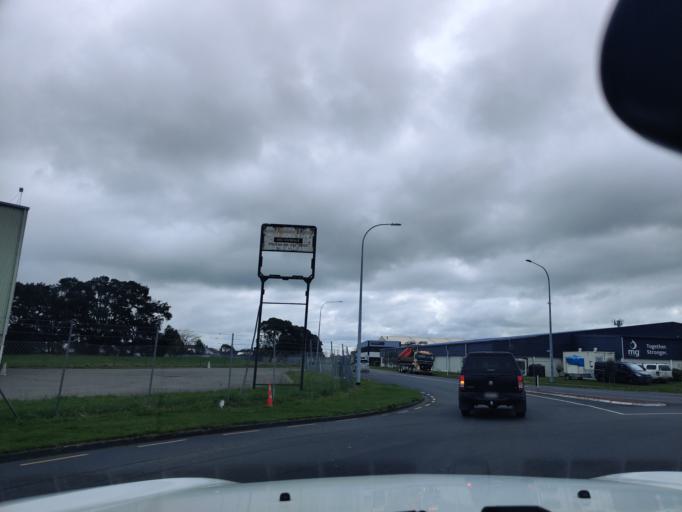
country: NZ
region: Manawatu-Wanganui
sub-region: Palmerston North City
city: Palmerston North
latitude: -40.3403
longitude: 175.6430
